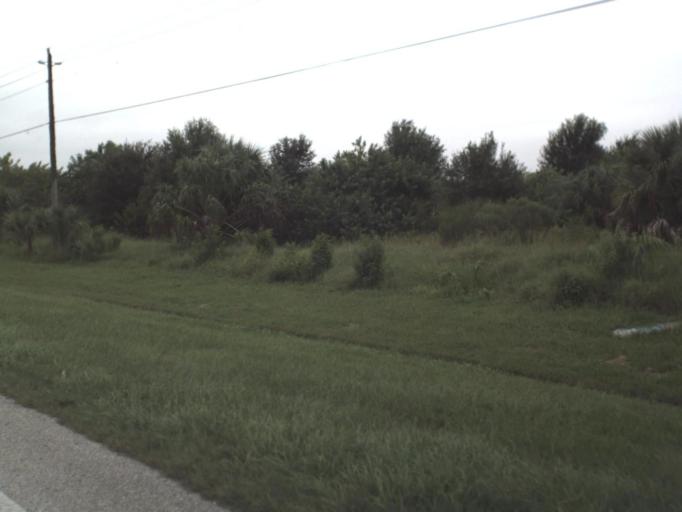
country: US
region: Florida
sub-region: Manatee County
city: Memphis
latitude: 27.6208
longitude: -82.5399
